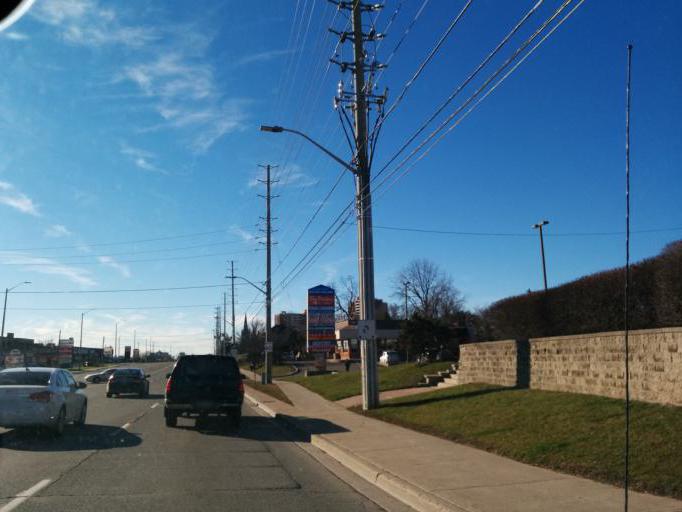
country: CA
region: Ontario
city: Etobicoke
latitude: 43.5976
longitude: -79.5970
